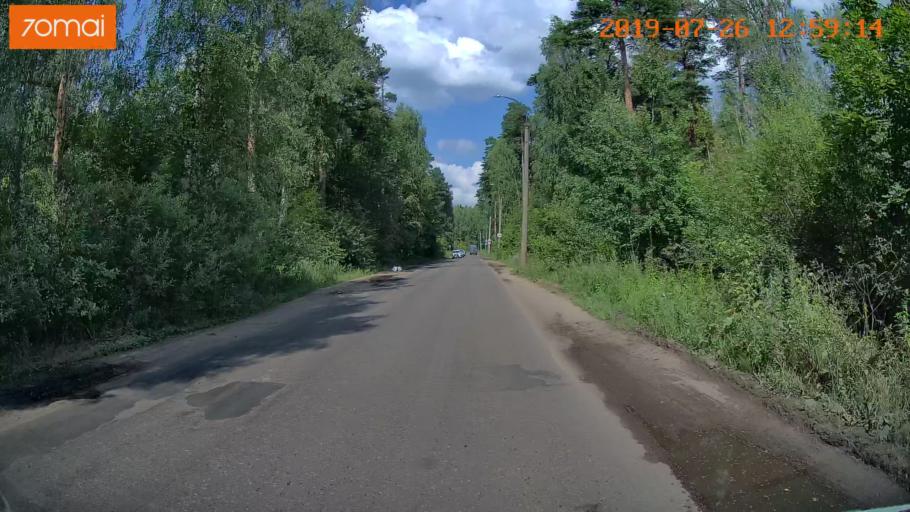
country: RU
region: Ivanovo
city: Bogorodskoye
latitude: 57.0277
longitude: 41.0209
